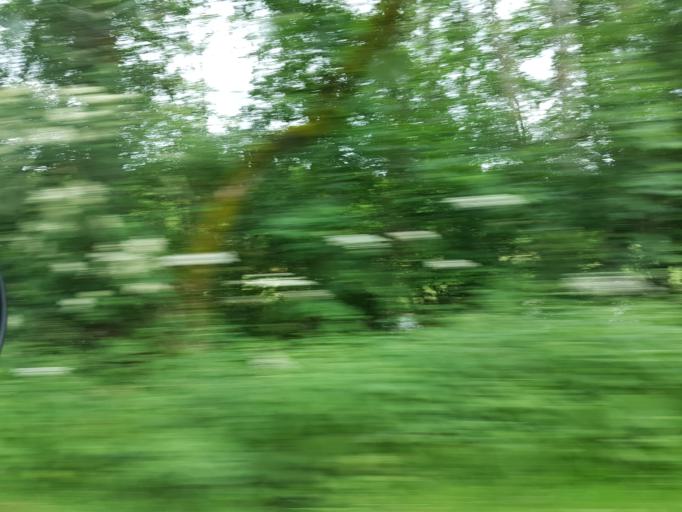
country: FR
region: Bourgogne
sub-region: Departement de la Nievre
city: Lormes
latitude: 47.1740
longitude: 3.8345
